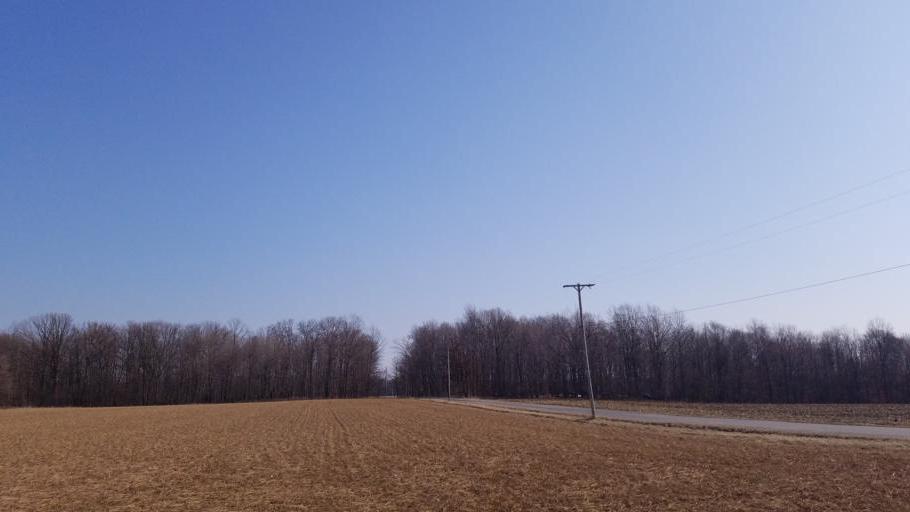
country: US
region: Ohio
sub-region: Richland County
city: Ontario
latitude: 40.8508
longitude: -82.5522
